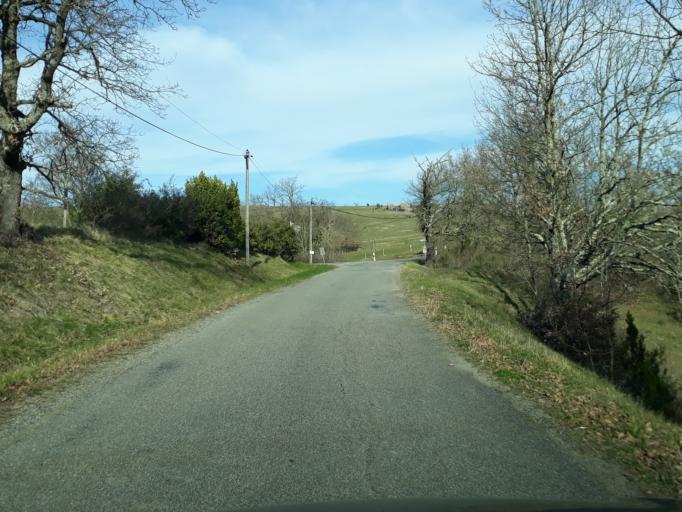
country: FR
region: Midi-Pyrenees
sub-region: Departement de la Haute-Garonne
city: Montesquieu-Volvestre
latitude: 43.1808
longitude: 1.2925
